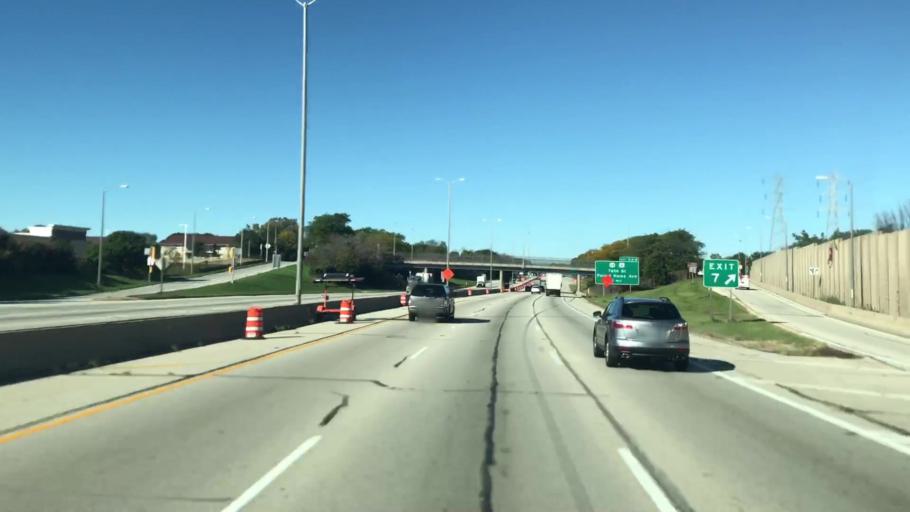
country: US
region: Wisconsin
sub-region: Milwaukee County
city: Greendale
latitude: 42.9624
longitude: -87.9858
